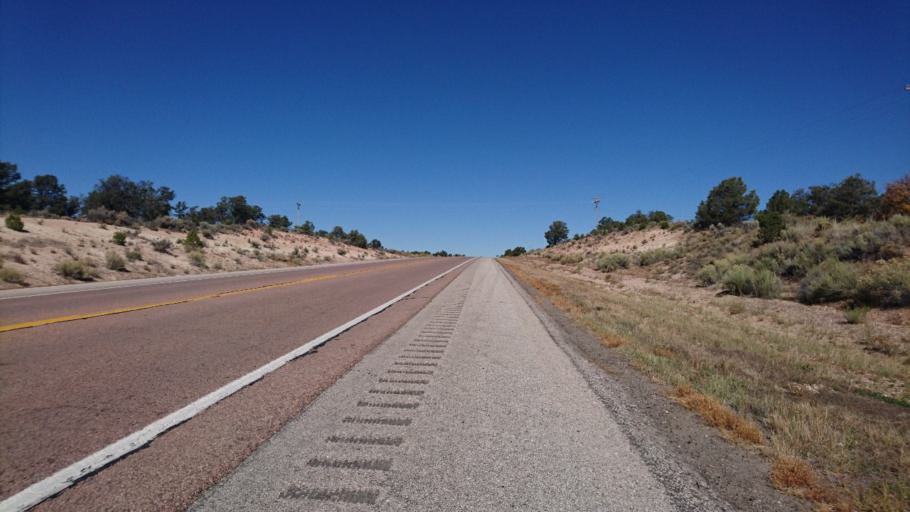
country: US
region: New Mexico
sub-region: McKinley County
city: Black Rock
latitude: 35.3070
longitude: -108.7576
